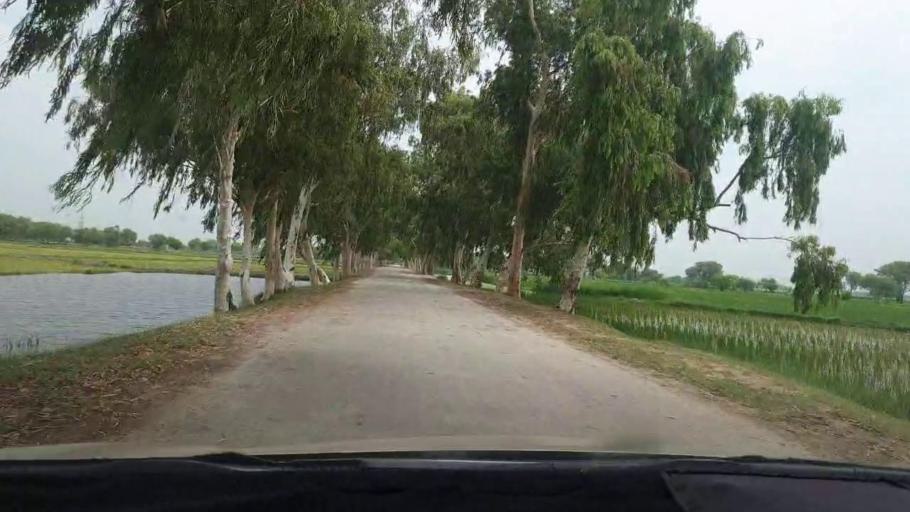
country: PK
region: Sindh
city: Ratodero
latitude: 27.7615
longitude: 68.3209
